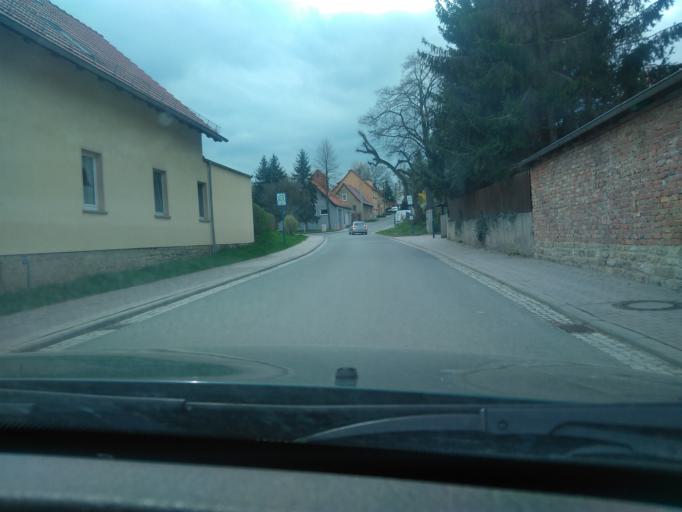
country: DE
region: Thuringia
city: Nohra
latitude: 50.9617
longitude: 11.2344
